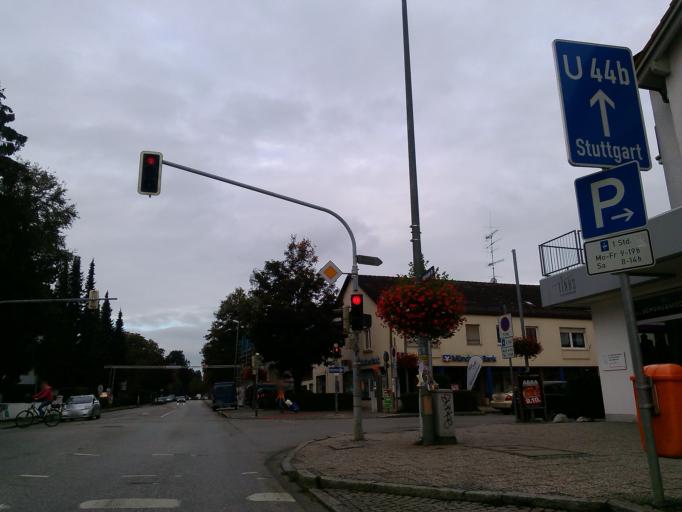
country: DE
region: Bavaria
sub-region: Upper Bavaria
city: Grobenzell
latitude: 48.1928
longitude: 11.3723
